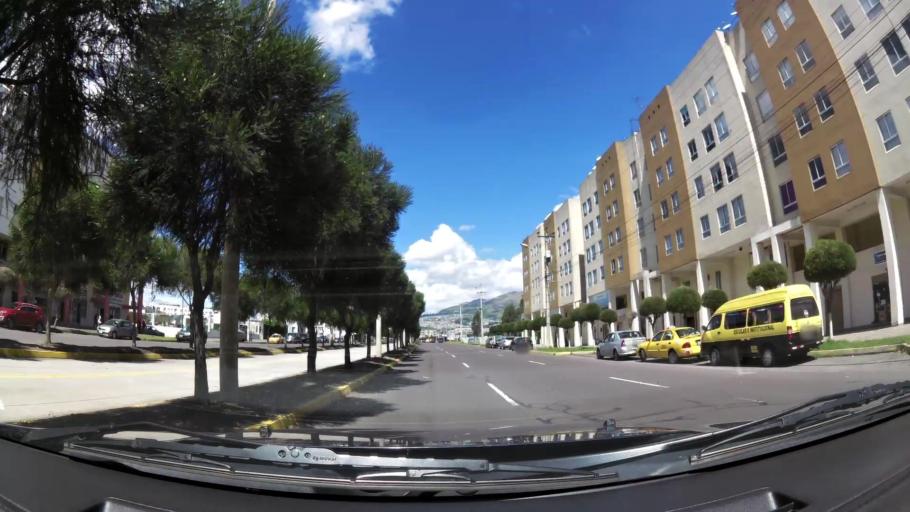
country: EC
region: Pichincha
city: Quito
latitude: -0.2951
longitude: -78.5489
